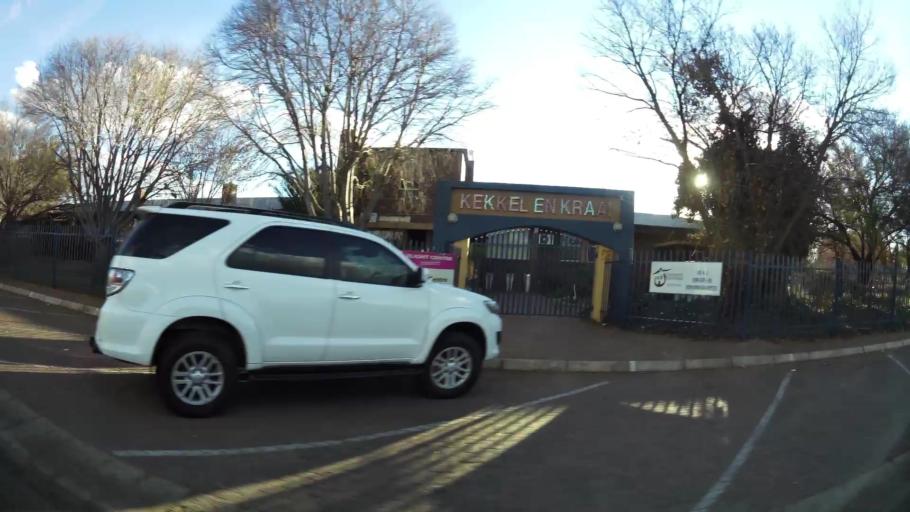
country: ZA
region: North-West
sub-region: Dr Kenneth Kaunda District Municipality
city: Potchefstroom
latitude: -26.7261
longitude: 27.0899
